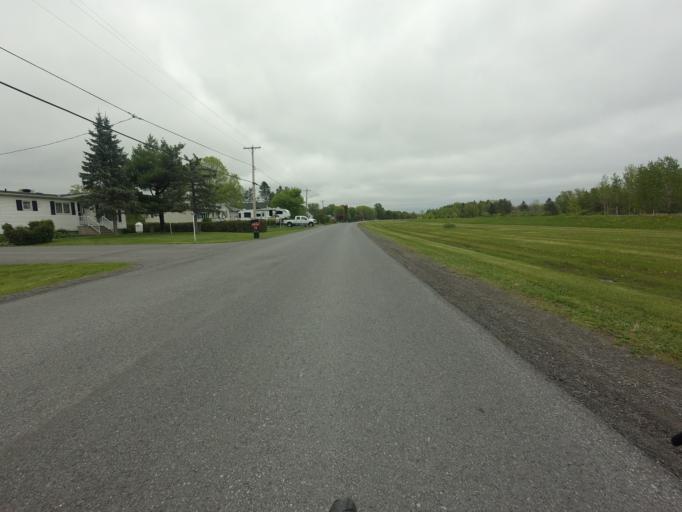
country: US
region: New York
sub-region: St. Lawrence County
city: Norfolk
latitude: 44.9374
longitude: -75.1174
